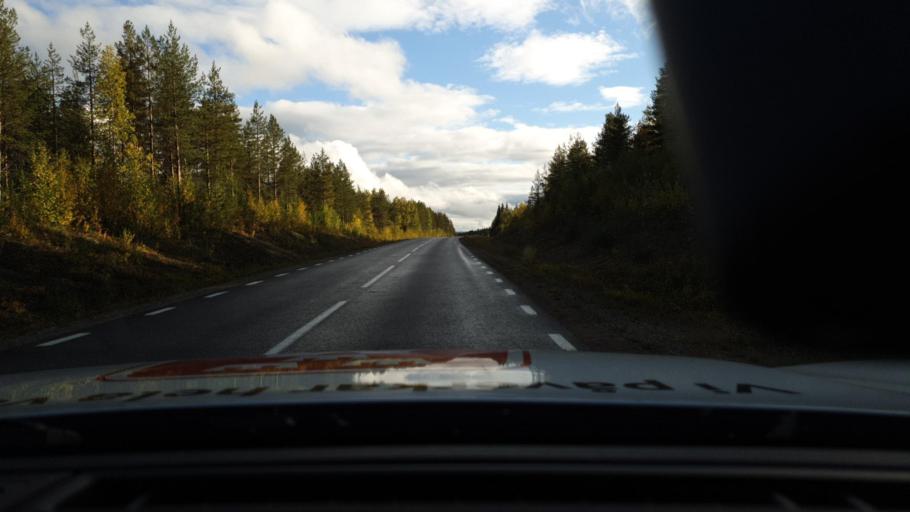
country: SE
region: Norrbotten
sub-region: Overkalix Kommun
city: OEverkalix
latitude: 66.7427
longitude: 22.6704
